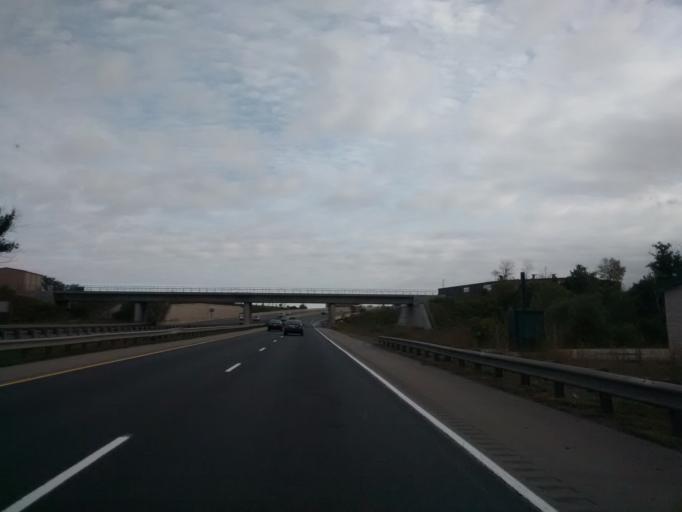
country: CA
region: Ontario
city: Hamilton
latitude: 43.2429
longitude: -79.7710
